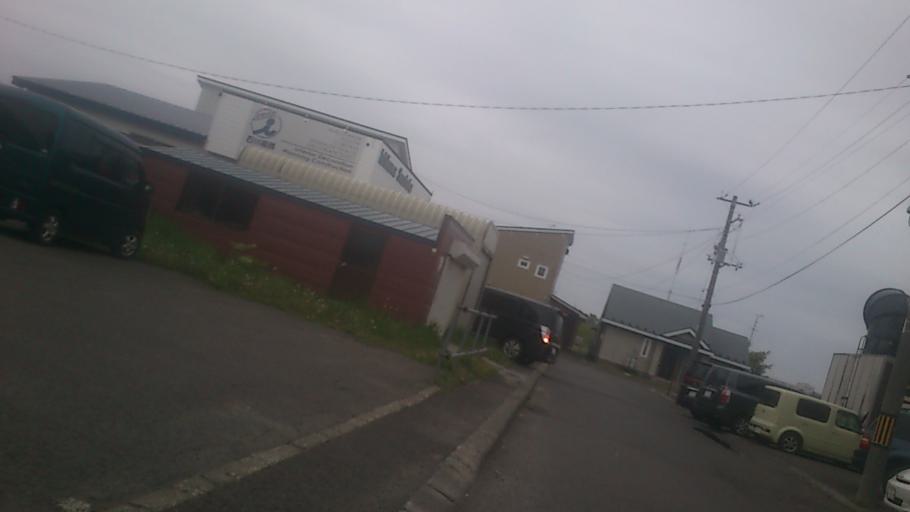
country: JP
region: Hokkaido
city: Kushiro
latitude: 42.9985
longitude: 144.4181
